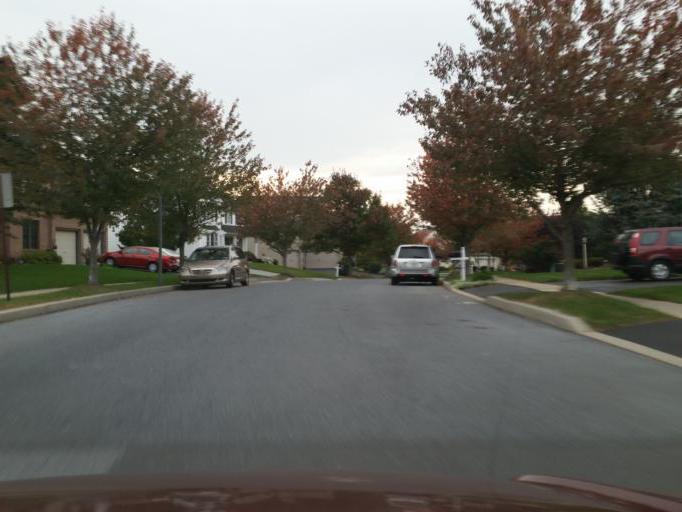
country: US
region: Pennsylvania
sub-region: Dauphin County
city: Hummelstown
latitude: 40.2416
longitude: -76.7210
